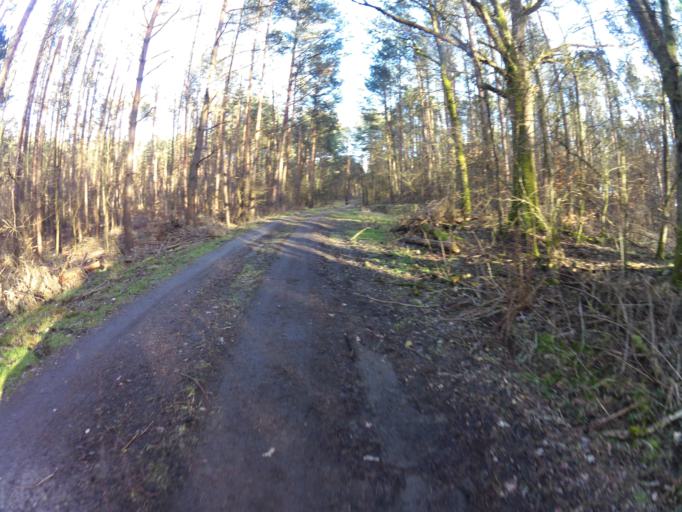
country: PL
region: West Pomeranian Voivodeship
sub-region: Powiat mysliborski
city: Debno
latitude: 52.8225
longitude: 14.7414
